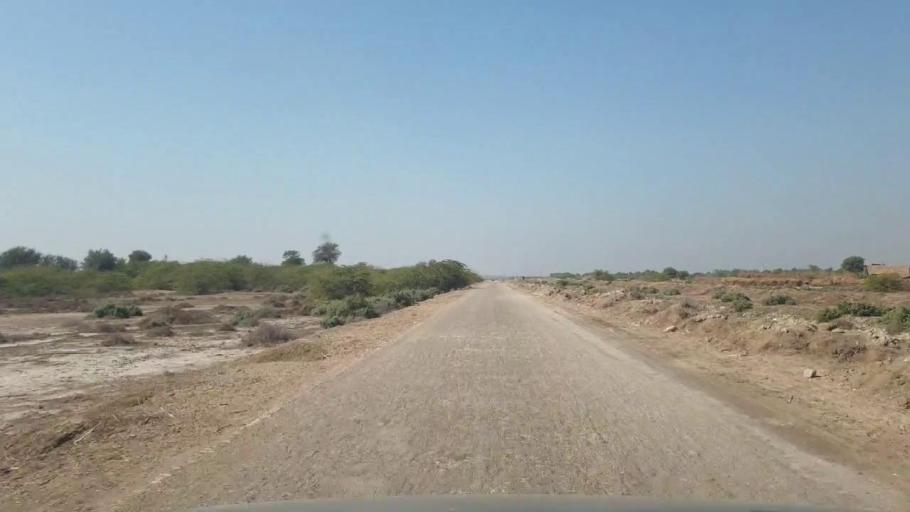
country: PK
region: Sindh
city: Digri
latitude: 25.2705
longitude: 69.2095
